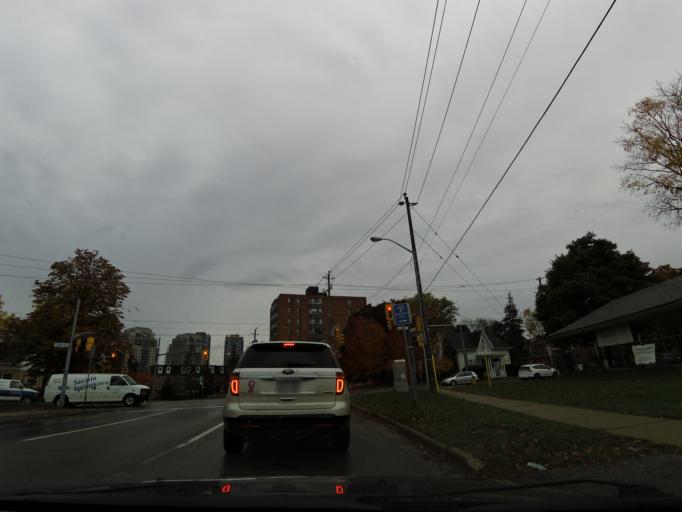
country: CA
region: Ontario
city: Waterloo
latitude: 43.4674
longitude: -80.5248
